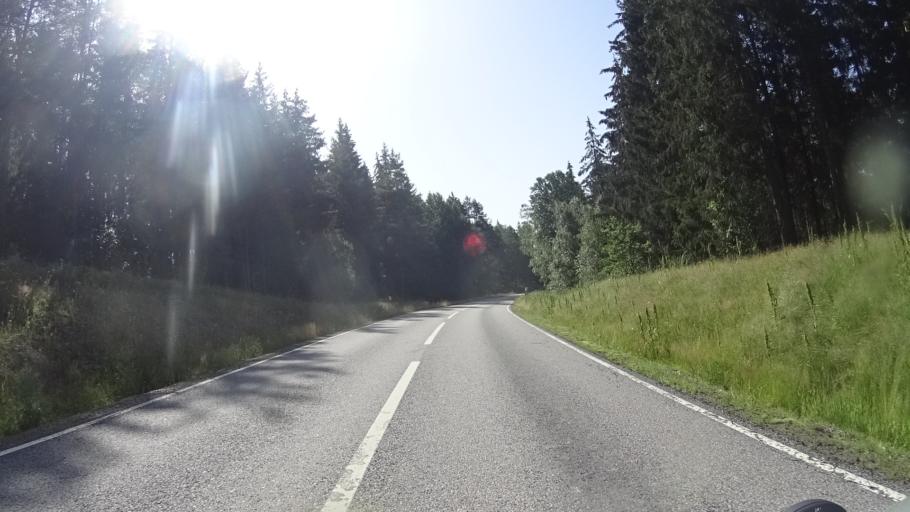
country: SE
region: Kalmar
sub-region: Vasterviks Kommun
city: Overum
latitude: 58.0433
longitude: 16.2202
